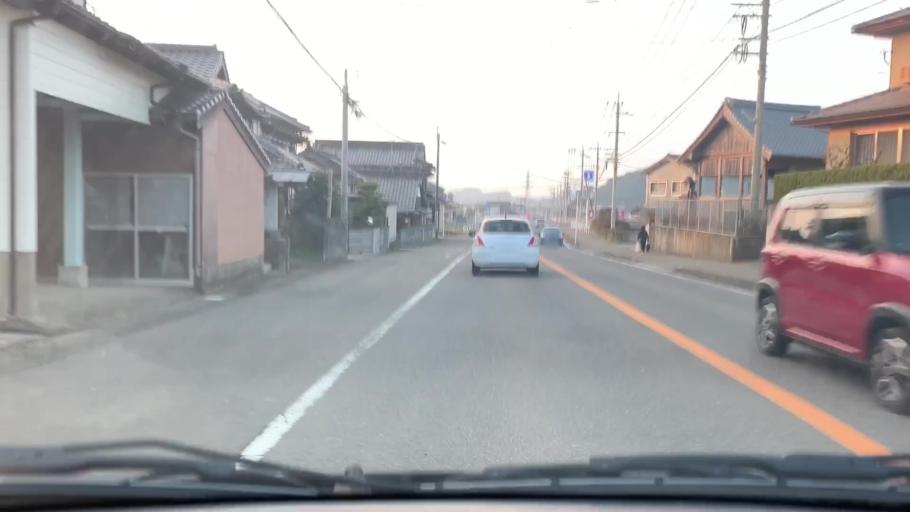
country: JP
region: Saga Prefecture
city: Imaricho-ko
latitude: 33.2677
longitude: 129.8998
